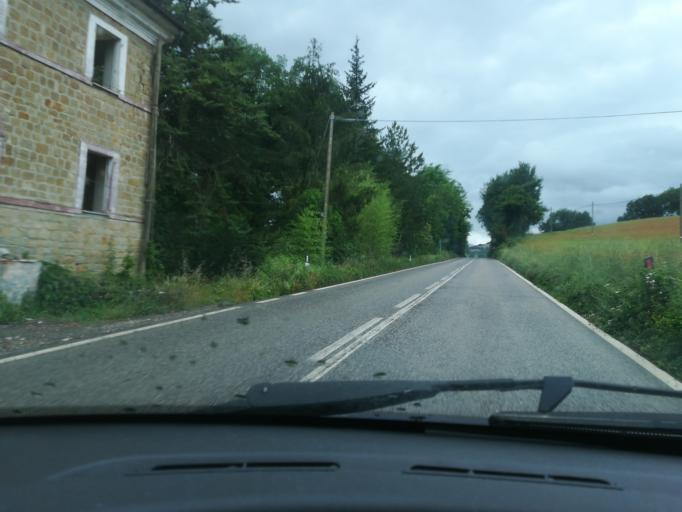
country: IT
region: The Marches
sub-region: Provincia di Macerata
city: San Ginesio
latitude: 43.0958
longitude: 13.3277
